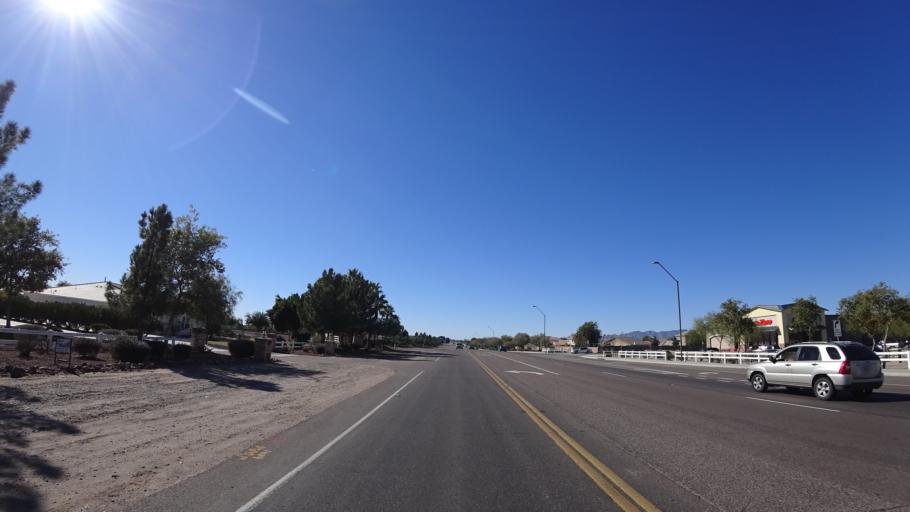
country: US
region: Arizona
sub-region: Maricopa County
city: Goodyear
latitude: 33.4356
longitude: -112.4129
